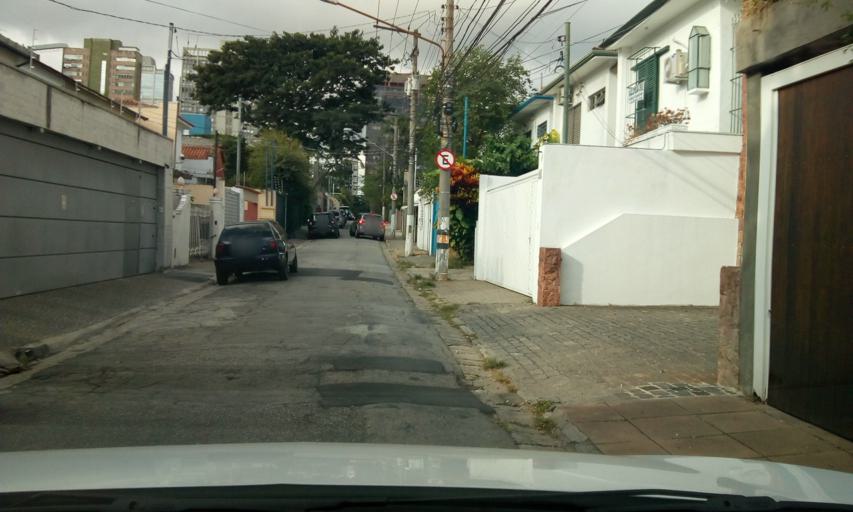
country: BR
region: Sao Paulo
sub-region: Sao Paulo
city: Sao Paulo
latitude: -23.5745
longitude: -46.6922
